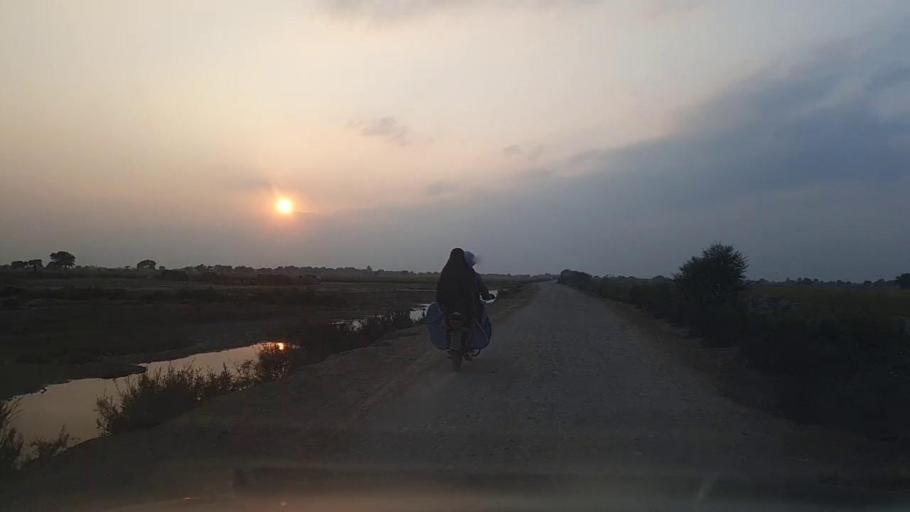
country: PK
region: Sindh
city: Jati
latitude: 24.5297
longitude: 68.3968
